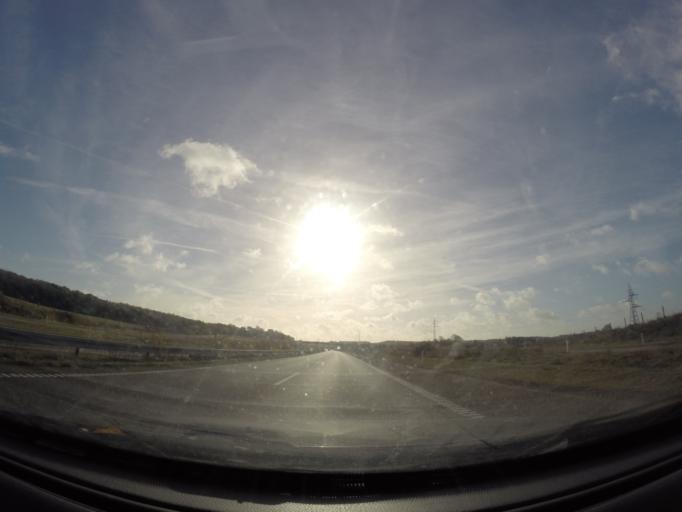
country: DK
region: South Denmark
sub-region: Svendborg Kommune
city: Svendborg
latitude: 55.1163
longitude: 10.5604
